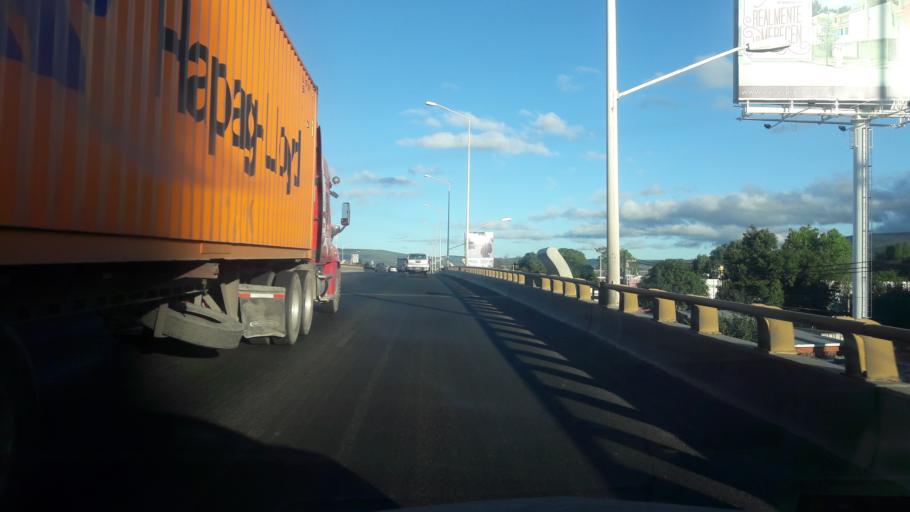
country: MX
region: Guanajuato
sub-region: Leon
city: Medina
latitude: 21.1707
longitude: -101.6568
